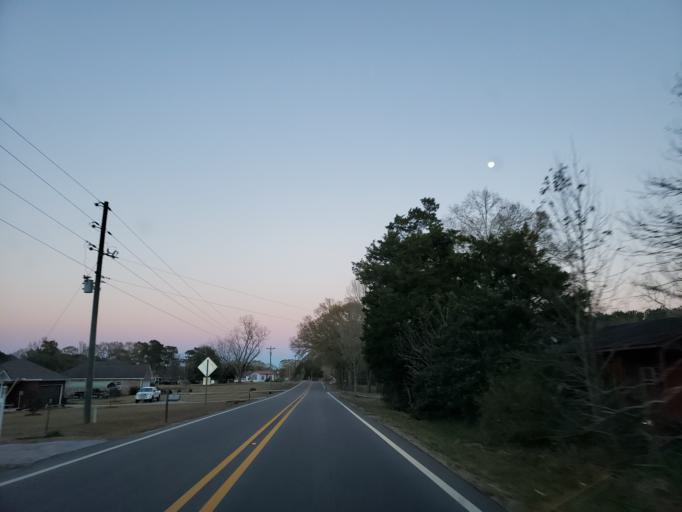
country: US
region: Mississippi
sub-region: Jones County
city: Ellisville
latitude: 31.5804
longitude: -89.2497
